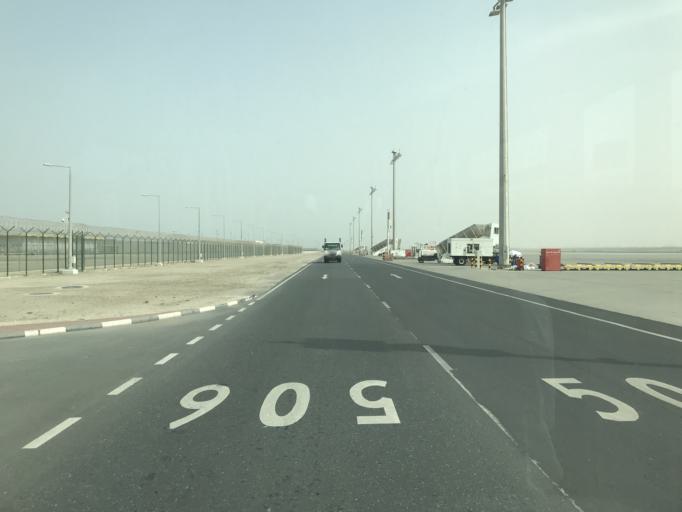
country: QA
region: Baladiyat ad Dawhah
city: Doha
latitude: 25.2757
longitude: 51.6003
